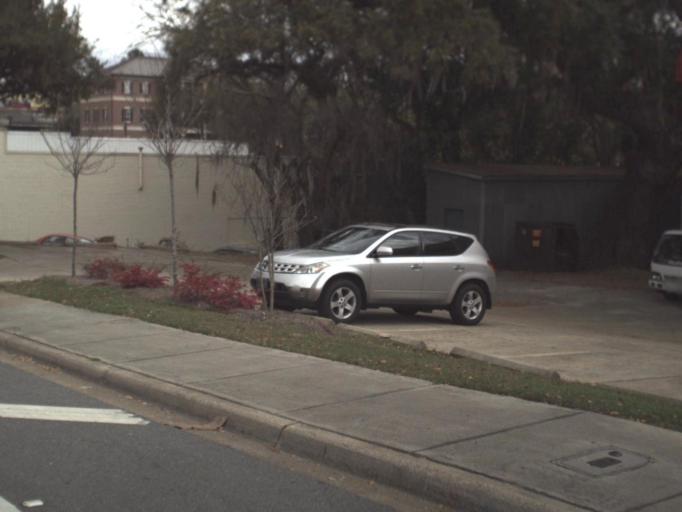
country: US
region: Florida
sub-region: Leon County
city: Tallahassee
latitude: 30.4496
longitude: -84.2806
